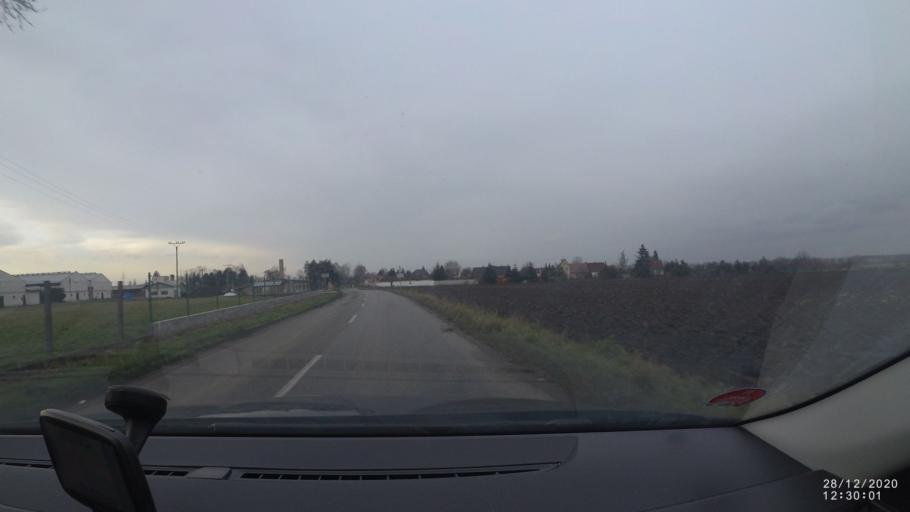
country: CZ
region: Central Bohemia
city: Kostelec nad Labem
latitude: 50.1995
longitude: 14.6030
